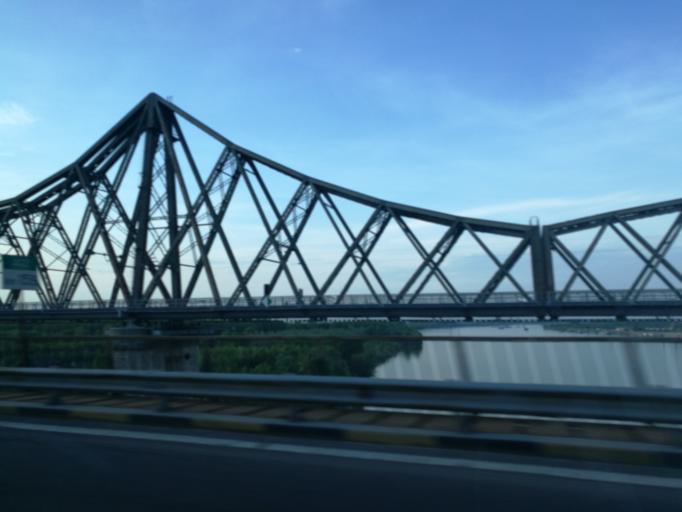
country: RO
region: Constanta
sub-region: Oras Cernavoda
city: Cernavoda
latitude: 44.3403
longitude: 28.0157
